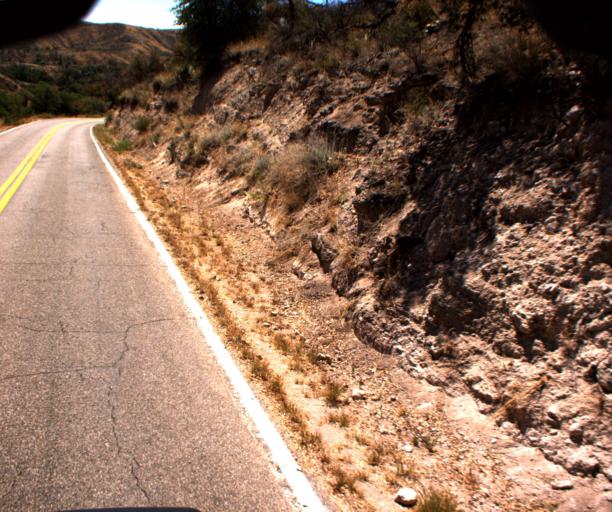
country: US
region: Arizona
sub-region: Santa Cruz County
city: Rio Rico
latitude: 31.3880
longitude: -111.0709
